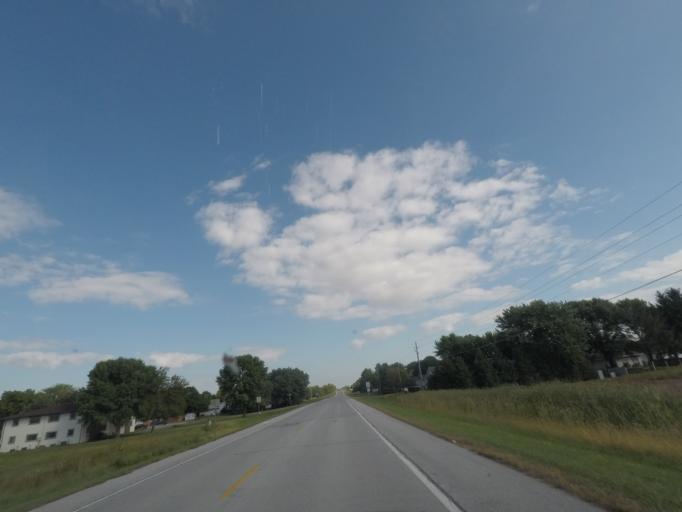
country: US
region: Iowa
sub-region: Story County
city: Nevada
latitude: 42.0004
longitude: -93.4446
